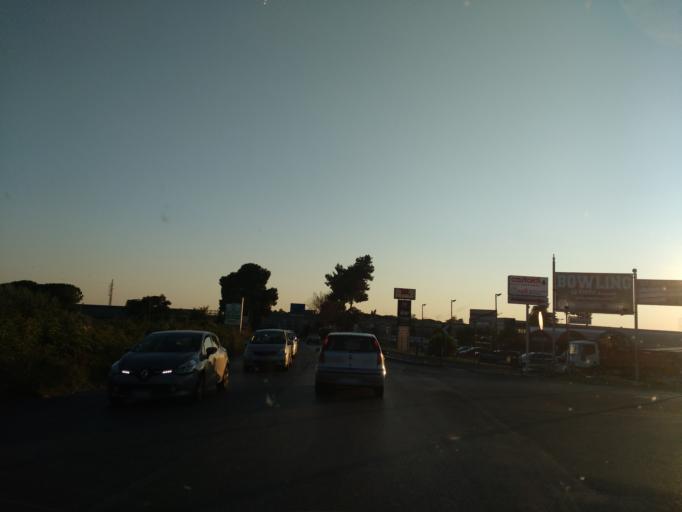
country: IT
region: Latium
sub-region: Citta metropolitana di Roma Capitale
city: Albuccione
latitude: 41.9545
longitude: 12.7054
